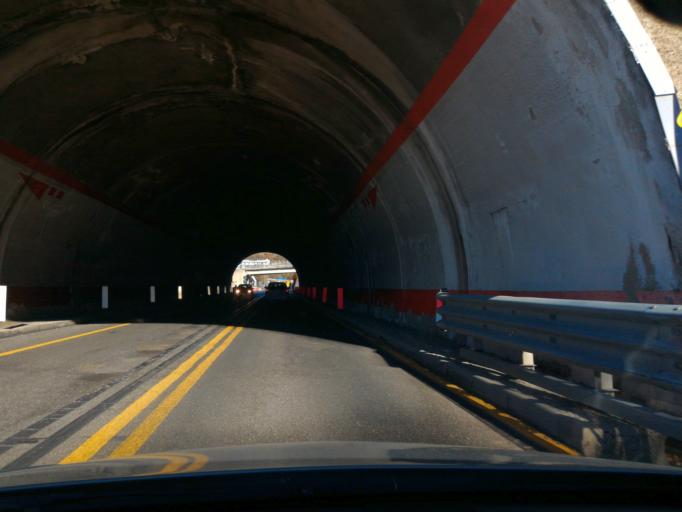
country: IT
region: Calabria
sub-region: Provincia di Cosenza
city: Spezzano Piccolo
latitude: 39.2919
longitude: 16.3453
